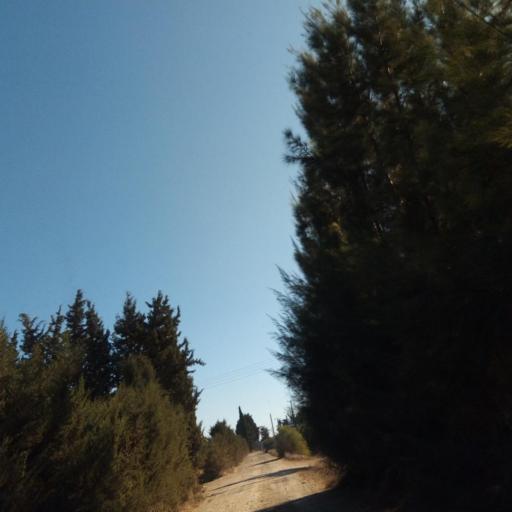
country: CY
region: Larnaka
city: Kolossi
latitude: 34.6491
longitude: 32.9398
